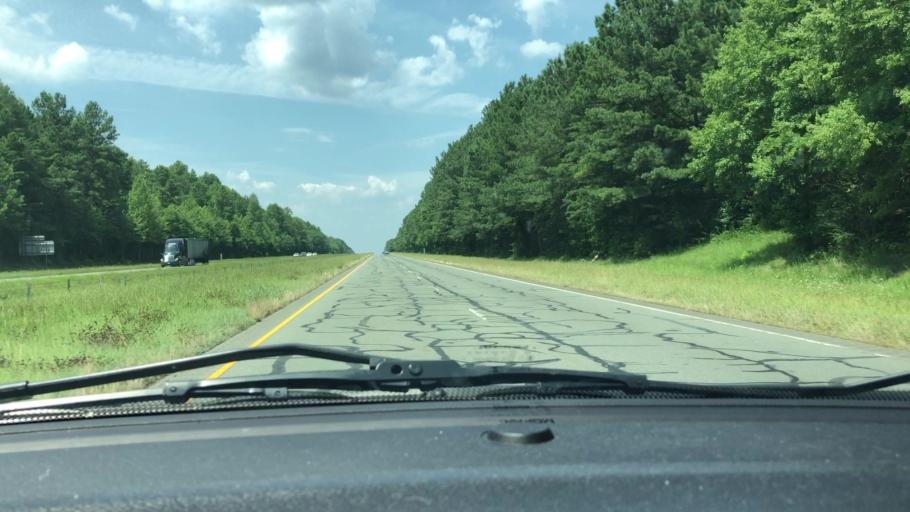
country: US
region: North Carolina
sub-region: Chatham County
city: Siler City
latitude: 35.7048
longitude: -79.4286
